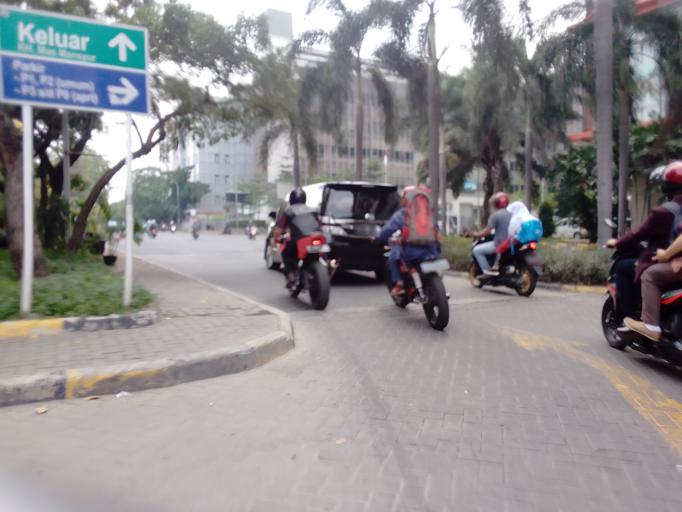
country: ID
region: Jakarta Raya
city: Jakarta
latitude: -6.1980
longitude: 106.8164
